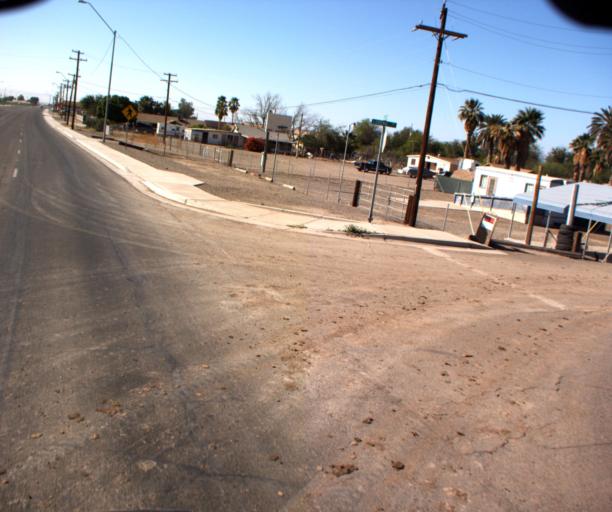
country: US
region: Arizona
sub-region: Yuma County
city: San Luis
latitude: 32.5636
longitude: -114.7849
